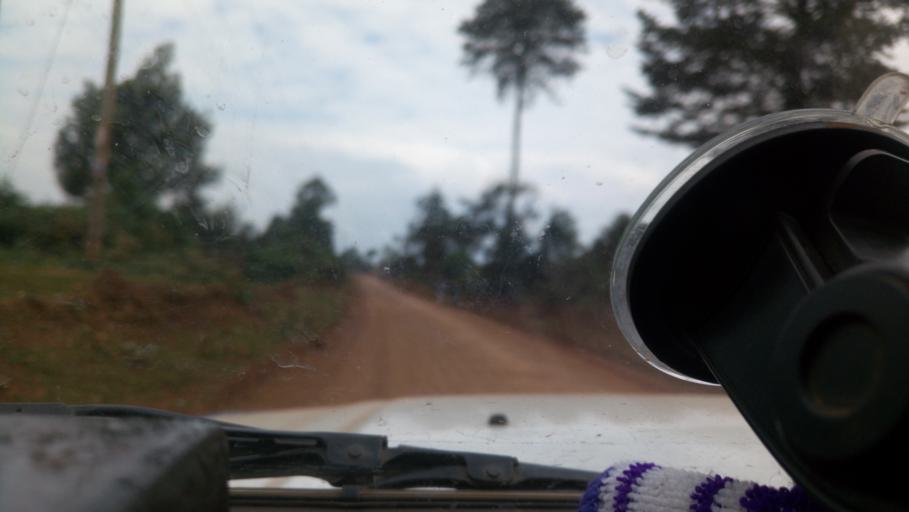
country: KE
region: Kericho
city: Litein
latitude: -0.5957
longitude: 35.1973
